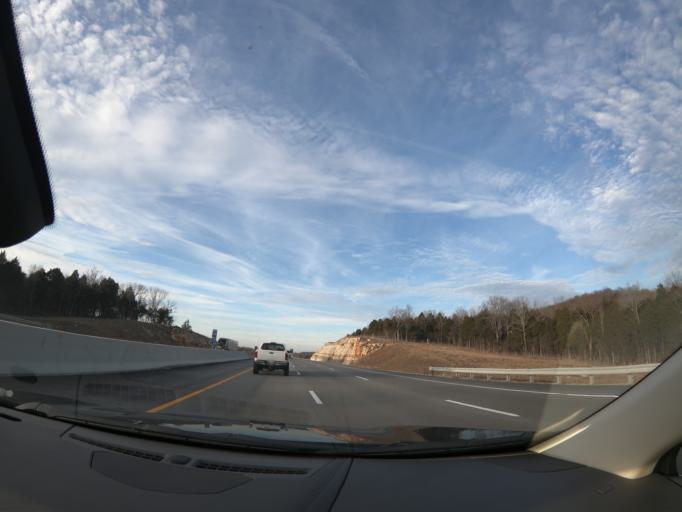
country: US
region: Kentucky
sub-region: Hart County
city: Munfordville
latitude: 37.4219
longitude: -85.8824
